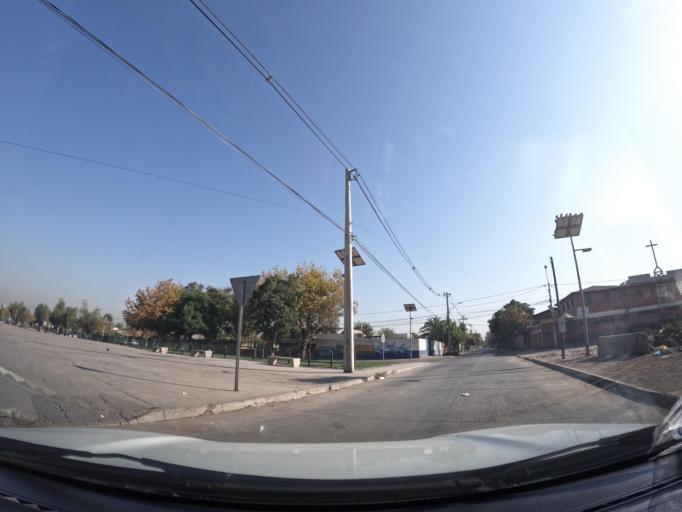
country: CL
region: Santiago Metropolitan
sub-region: Provincia de Santiago
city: Villa Presidente Frei, Nunoa, Santiago, Chile
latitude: -33.5113
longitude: -70.5697
